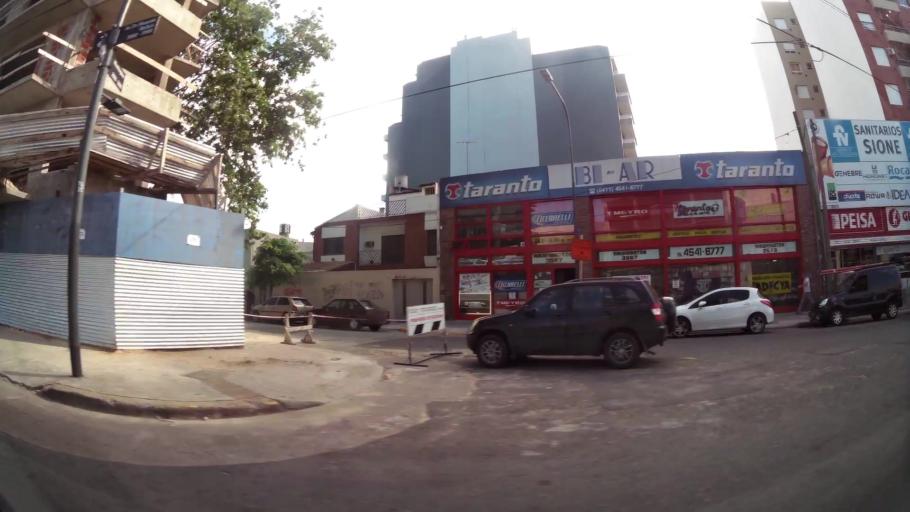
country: AR
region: Buenos Aires F.D.
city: Colegiales
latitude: -34.5561
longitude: -58.4804
